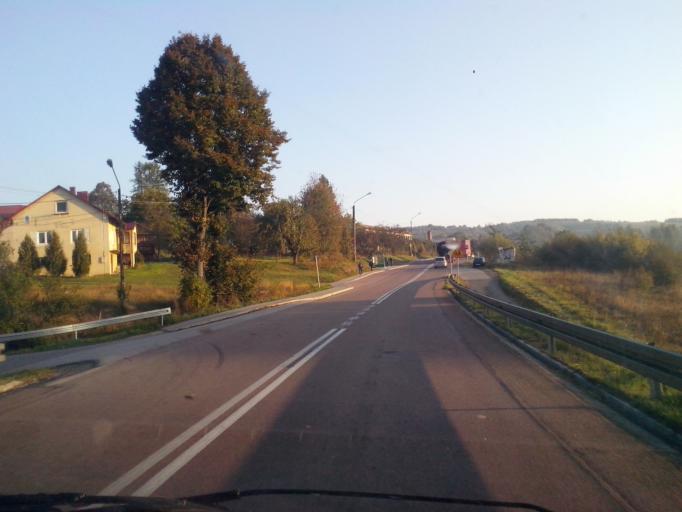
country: PL
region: Subcarpathian Voivodeship
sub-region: Powiat brzozowski
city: Golcowa
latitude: 49.8121
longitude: 22.0407
